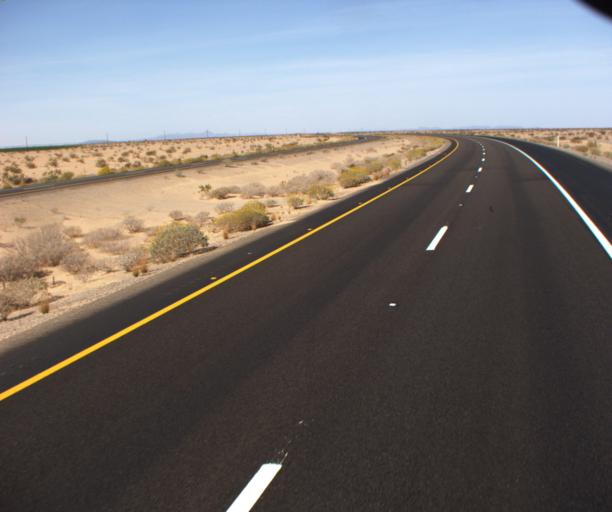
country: US
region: Arizona
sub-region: Yuma County
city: Somerton
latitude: 32.5051
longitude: -114.5581
